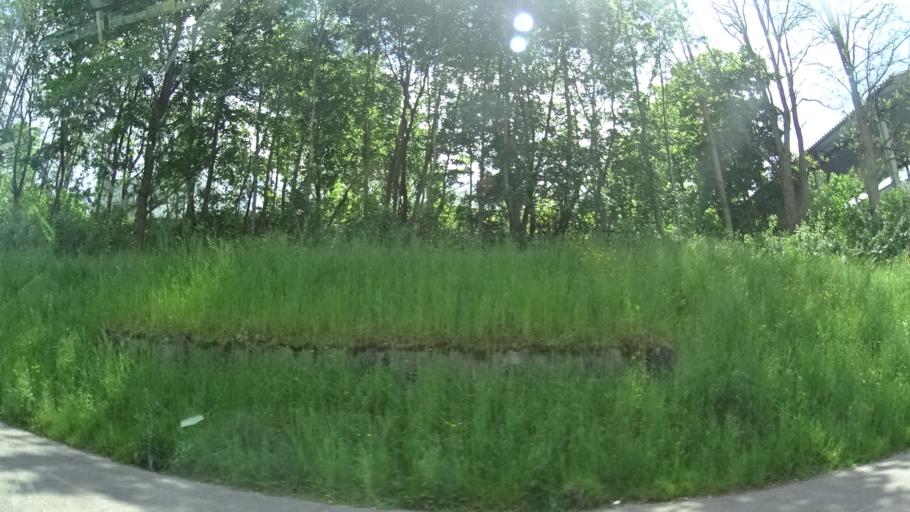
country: DE
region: Thuringia
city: Suhl
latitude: 50.6052
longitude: 10.6794
